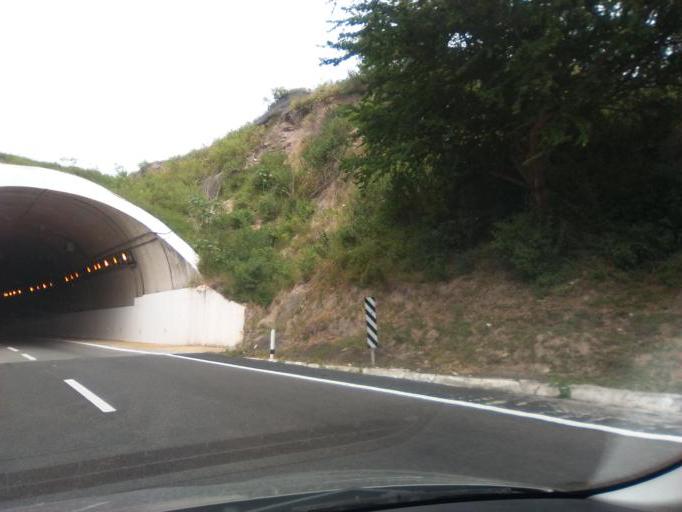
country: MX
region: Guerrero
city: Zumpango del Rio
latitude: 17.6644
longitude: -99.4948
